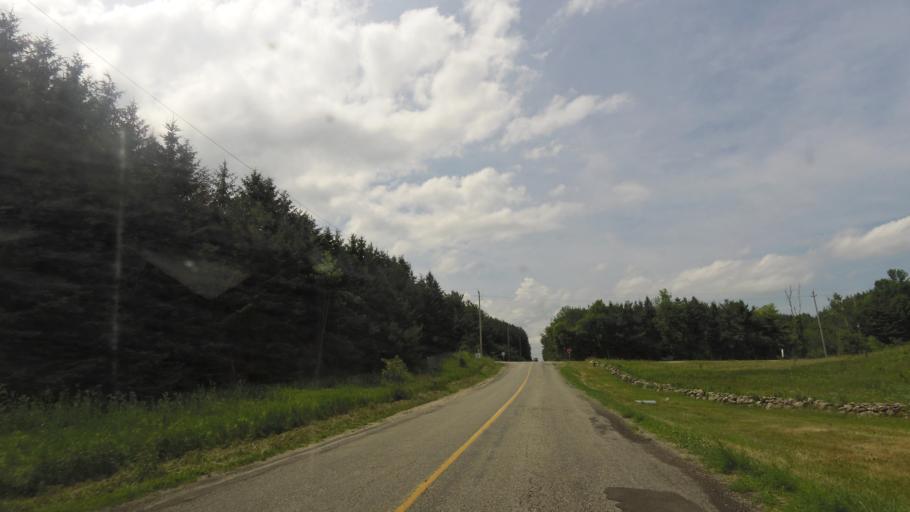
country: CA
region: Ontario
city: Orangeville
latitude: 43.8784
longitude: -79.9247
